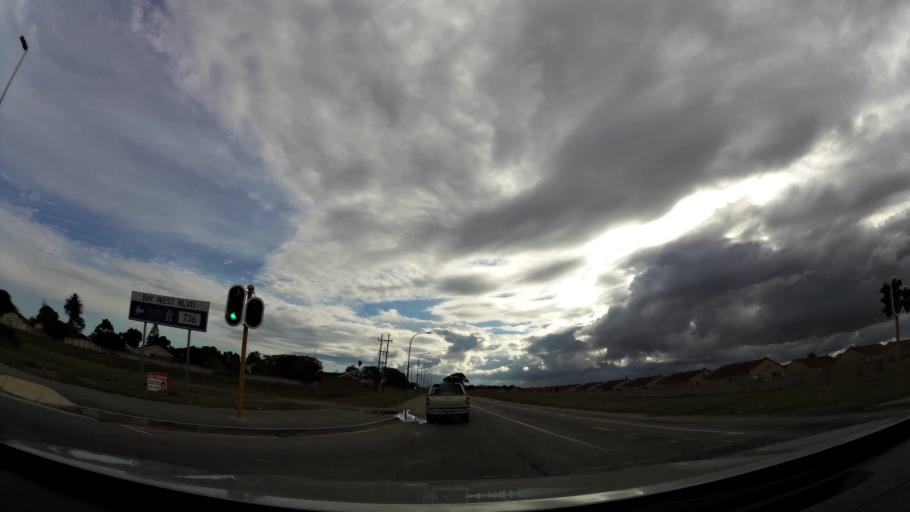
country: ZA
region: Eastern Cape
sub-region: Nelson Mandela Bay Metropolitan Municipality
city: Port Elizabeth
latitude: -33.9352
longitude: 25.4714
